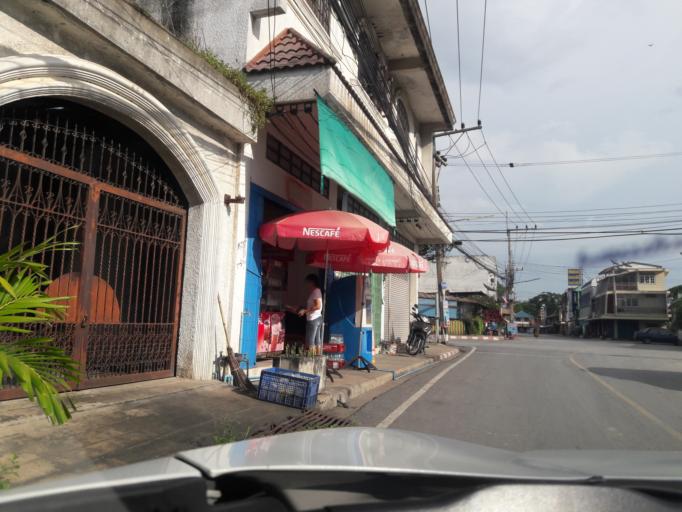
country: TH
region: Lop Buri
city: Ban Mi
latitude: 15.0429
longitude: 100.5384
